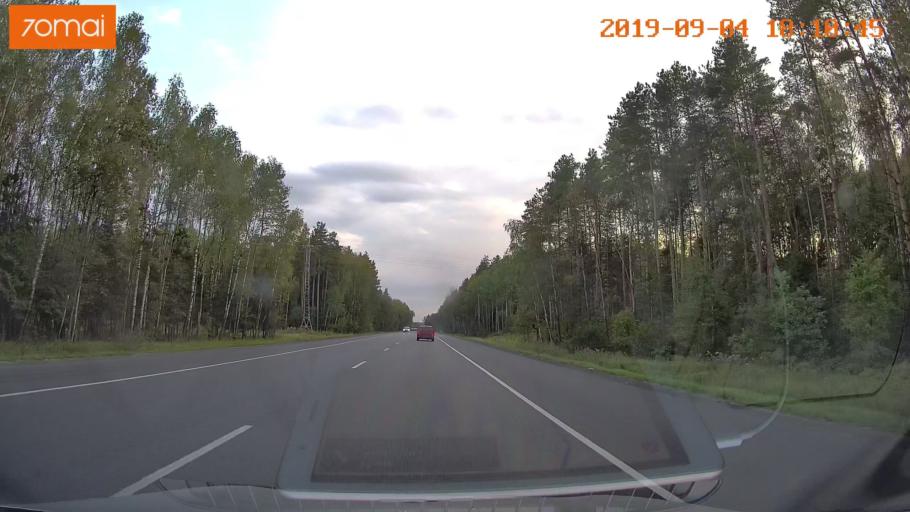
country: RU
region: Moskovskaya
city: Lopatinskiy
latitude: 55.3846
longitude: 38.7618
